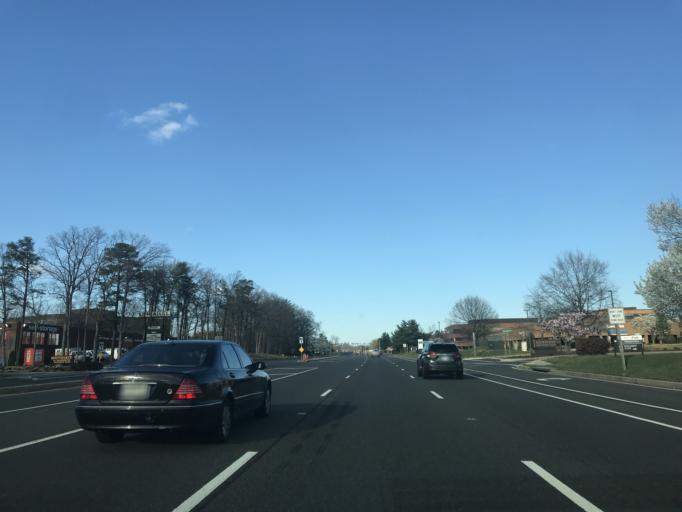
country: US
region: Maryland
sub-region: Prince George's County
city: Springdale
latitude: 38.9505
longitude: -76.8378
